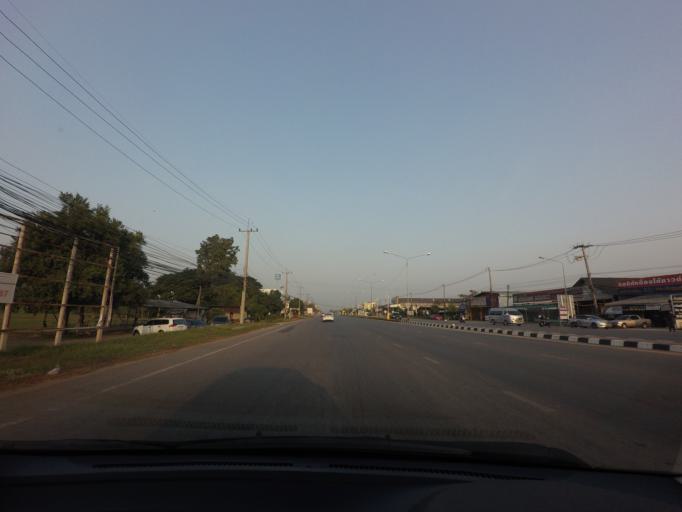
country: TH
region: Sukhothai
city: Sukhothai
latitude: 17.0119
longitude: 99.8374
